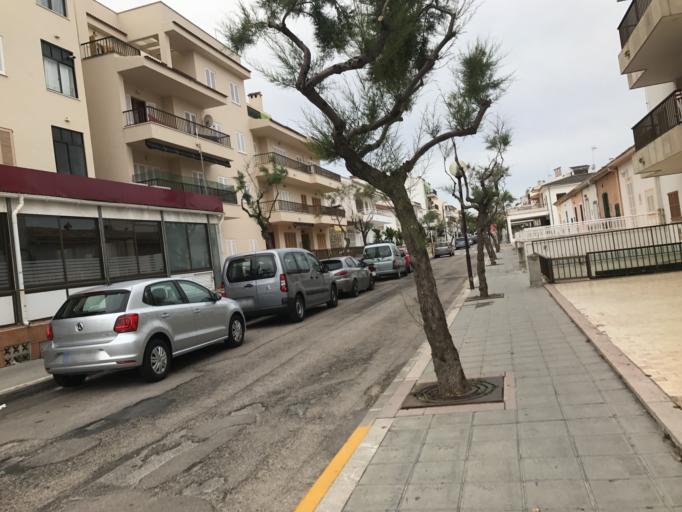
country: ES
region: Balearic Islands
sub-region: Illes Balears
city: Port d'Alcudia
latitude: 39.7652
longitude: 3.1565
